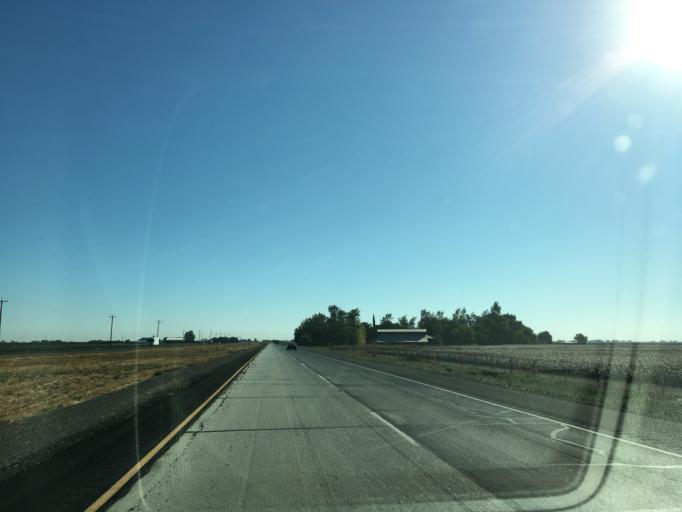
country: US
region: California
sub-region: Merced County
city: Dos Palos
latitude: 37.0514
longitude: -120.5709
